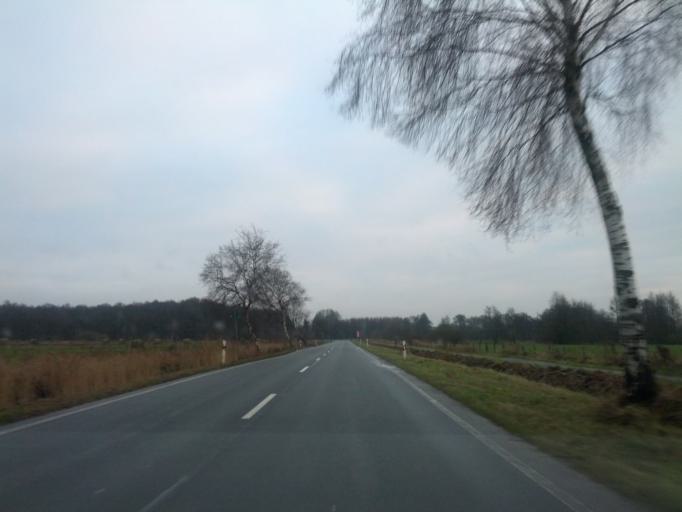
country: DE
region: Lower Saxony
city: Neu Wulmstorf
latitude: 53.4883
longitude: 9.7804
